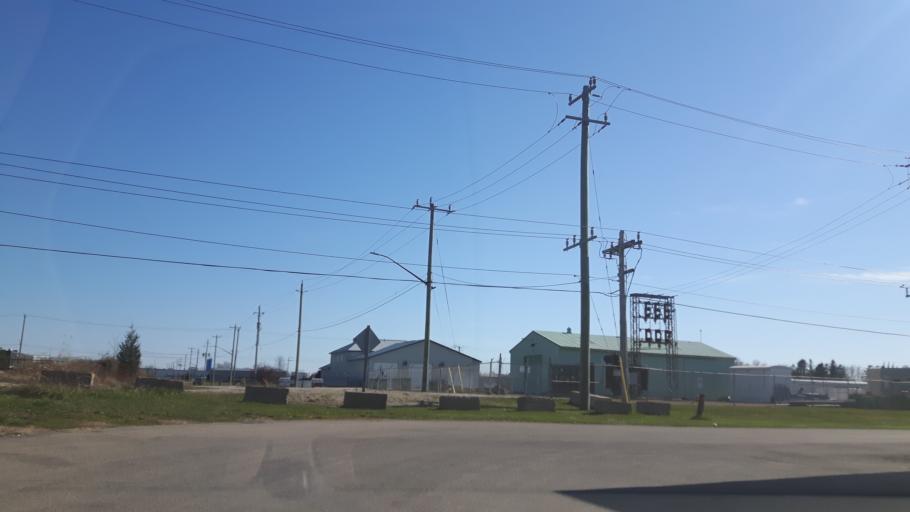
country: CA
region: Ontario
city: Goderich
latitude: 43.7283
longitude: -81.7030
